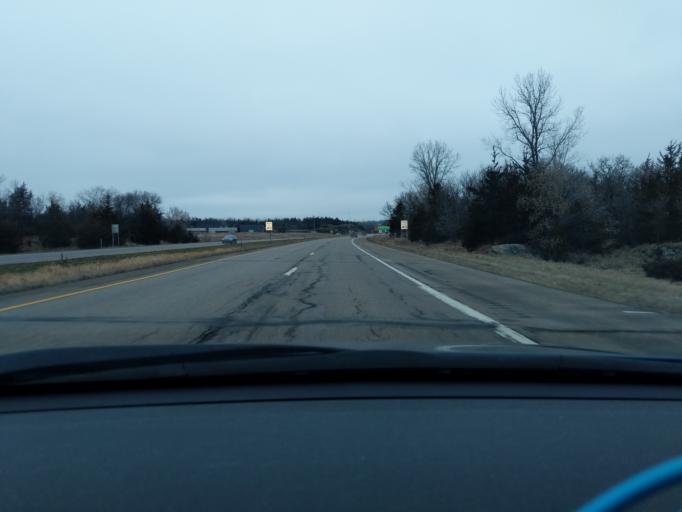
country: US
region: Minnesota
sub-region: Yellow Medicine County
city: Granite Falls
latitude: 44.7986
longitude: -95.5481
